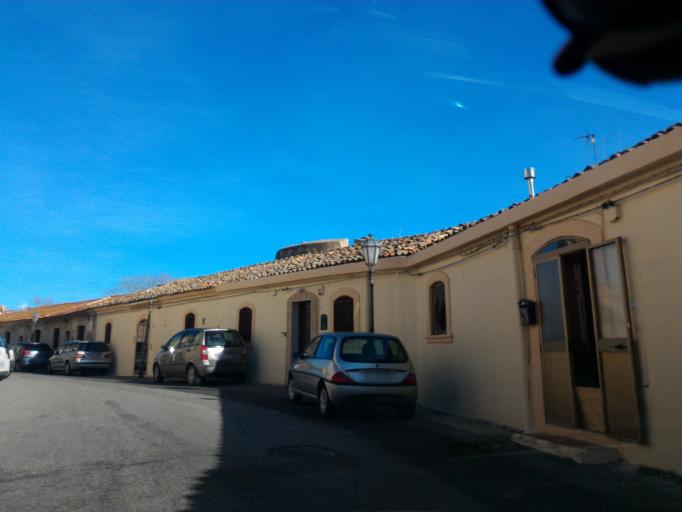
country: IT
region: Calabria
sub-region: Provincia di Crotone
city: Crotone
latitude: 39.0807
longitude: 17.1312
